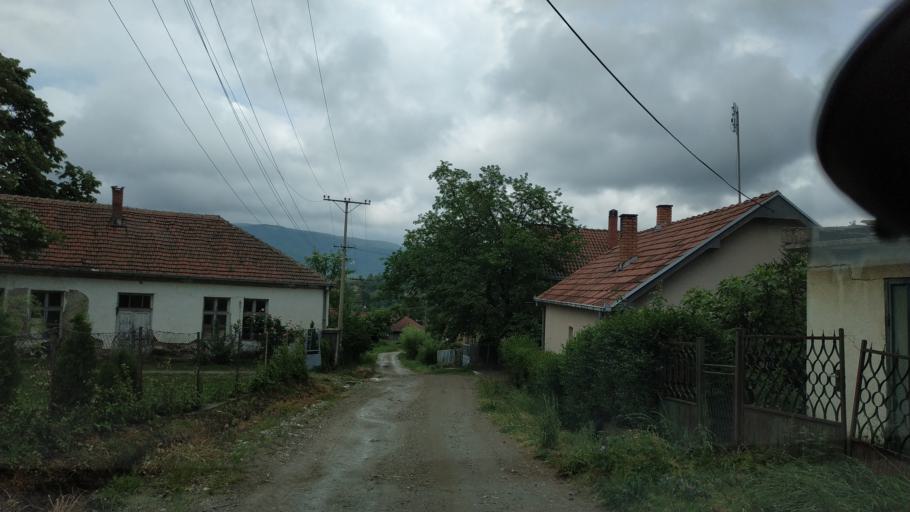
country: RS
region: Central Serbia
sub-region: Toplicki Okrug
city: Prokuplje
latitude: 43.4003
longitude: 21.5496
